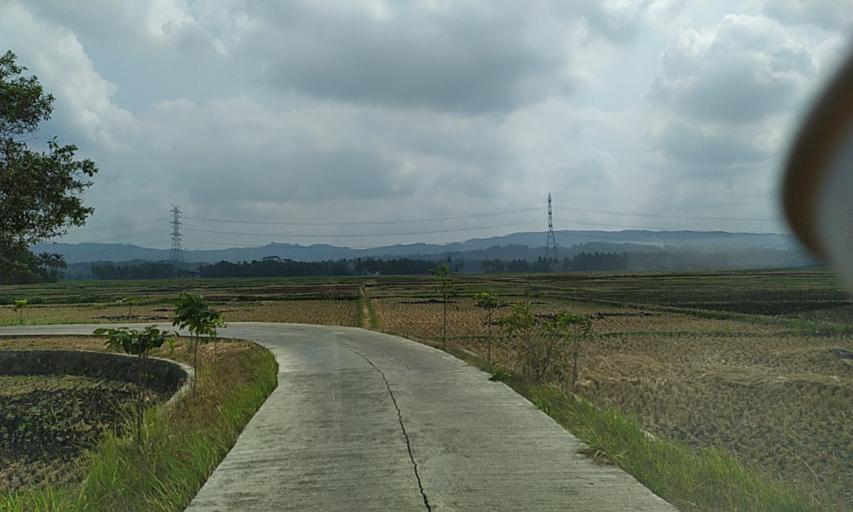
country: ID
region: Central Java
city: Kauman
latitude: -7.4724
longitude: 108.7791
